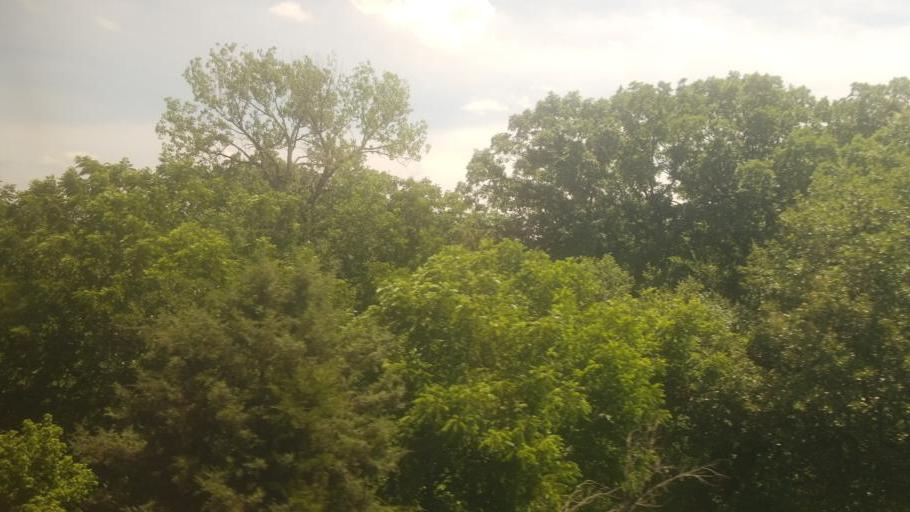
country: US
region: Missouri
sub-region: Linn County
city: Marceline
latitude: 39.8701
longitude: -92.7769
